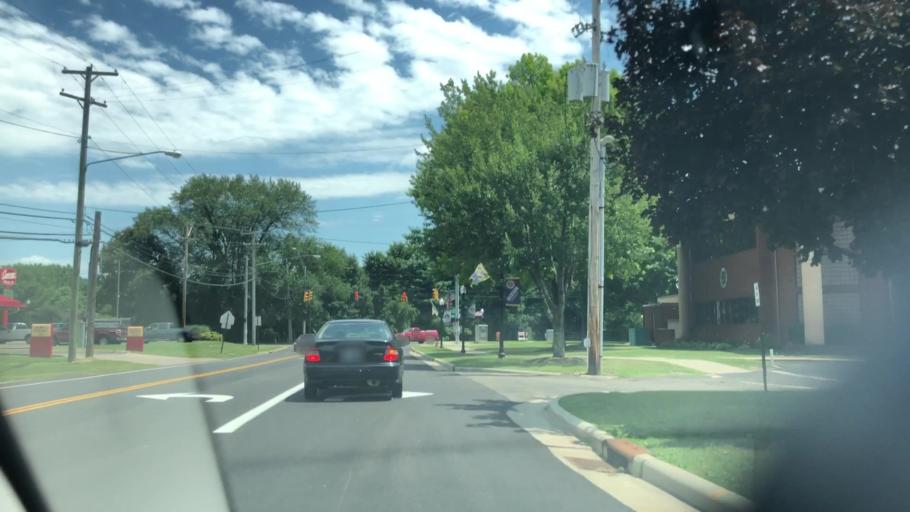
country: US
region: Ohio
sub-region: Summit County
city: Greensburg
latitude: 40.8655
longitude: -81.4854
